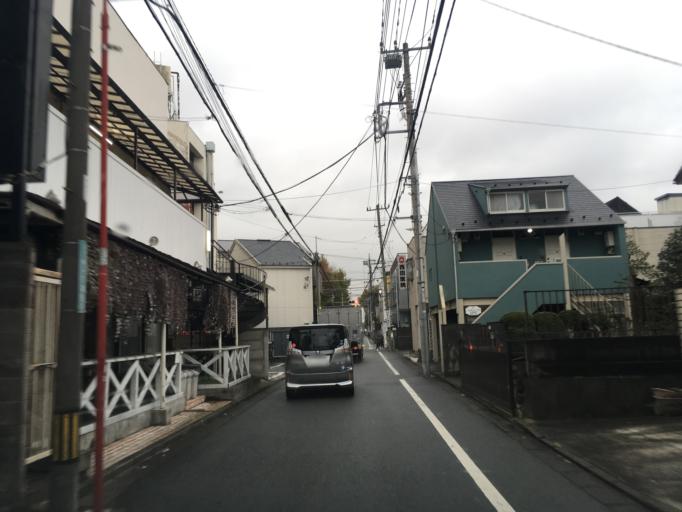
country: JP
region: Tokyo
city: Kokubunji
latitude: 35.6966
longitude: 139.4411
